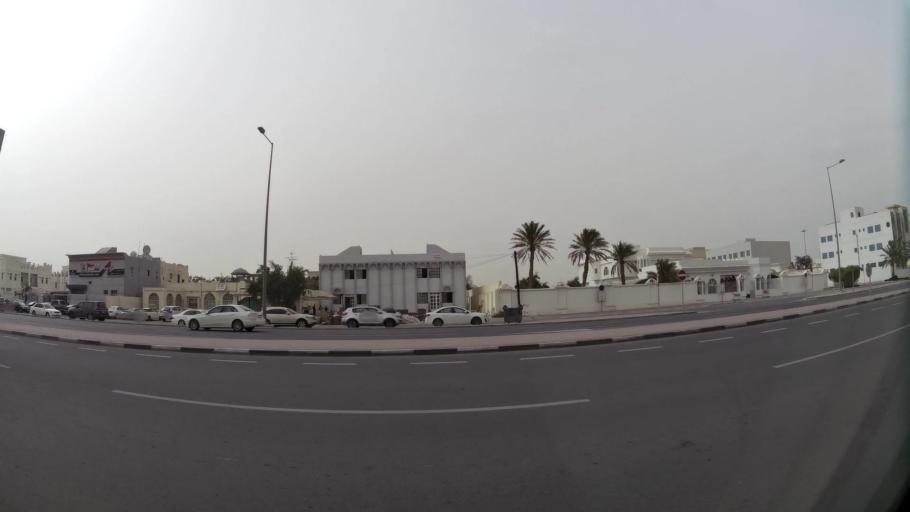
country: QA
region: Baladiyat ad Dawhah
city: Doha
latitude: 25.2579
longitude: 51.4983
